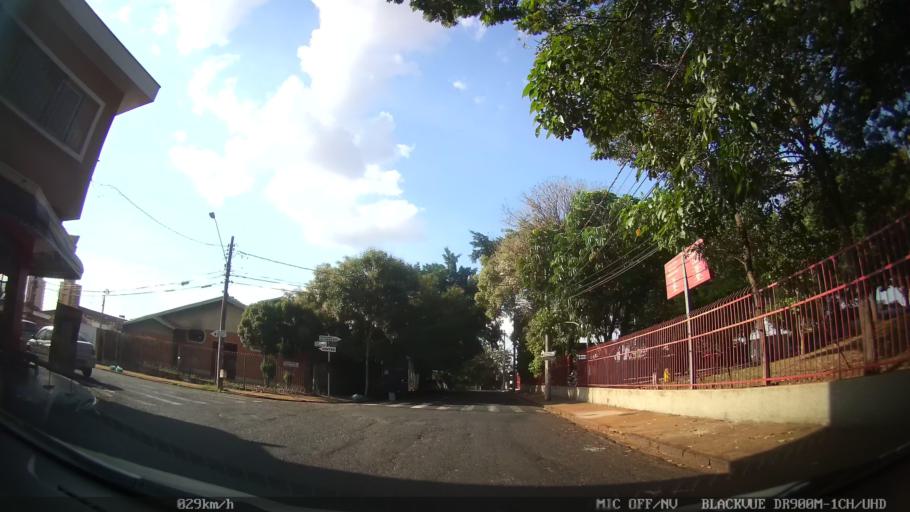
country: BR
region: Sao Paulo
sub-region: Ribeirao Preto
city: Ribeirao Preto
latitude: -21.1699
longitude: -47.8004
